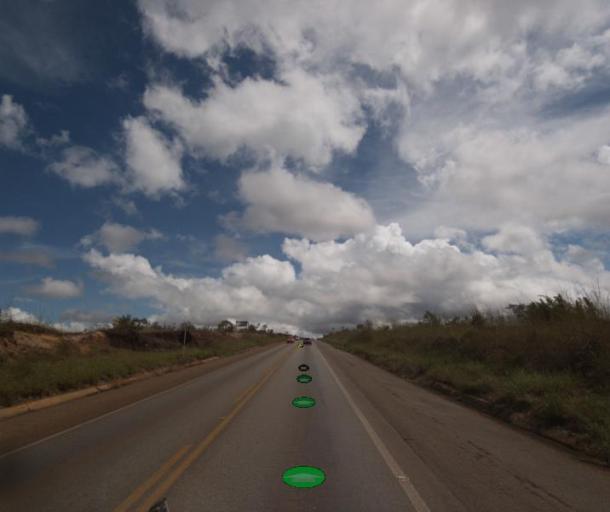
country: BR
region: Federal District
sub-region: Brasilia
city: Brasilia
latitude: -15.7424
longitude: -48.3764
